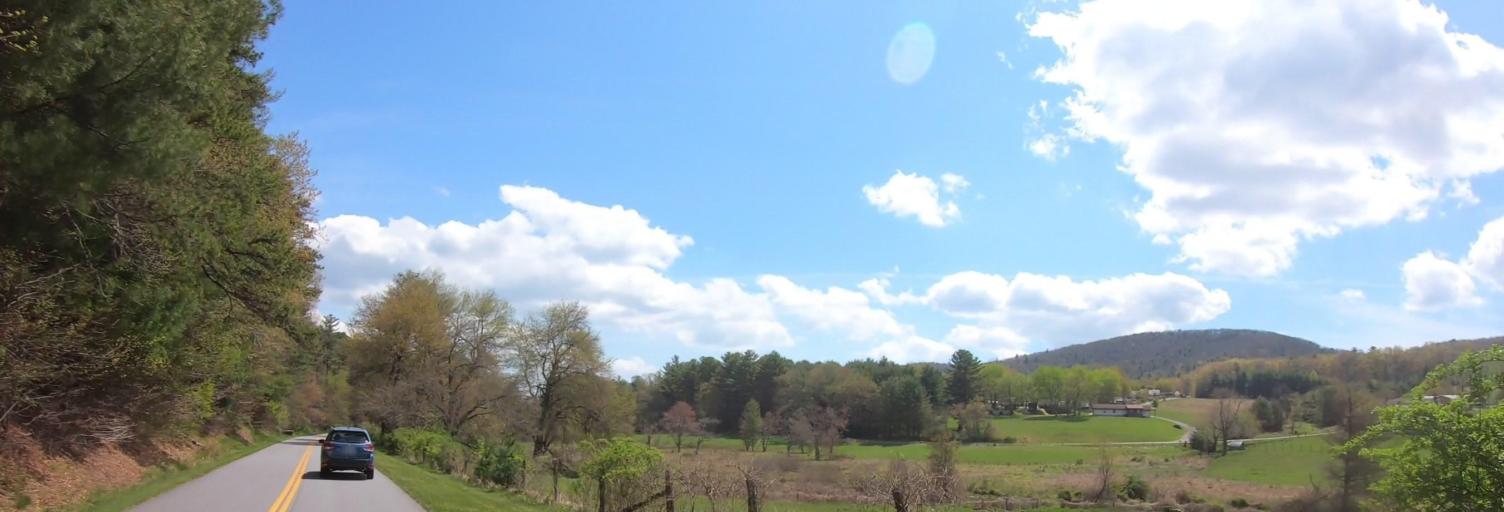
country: US
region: North Carolina
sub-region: Surry County
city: Thurmond
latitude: 36.5042
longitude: -80.9493
